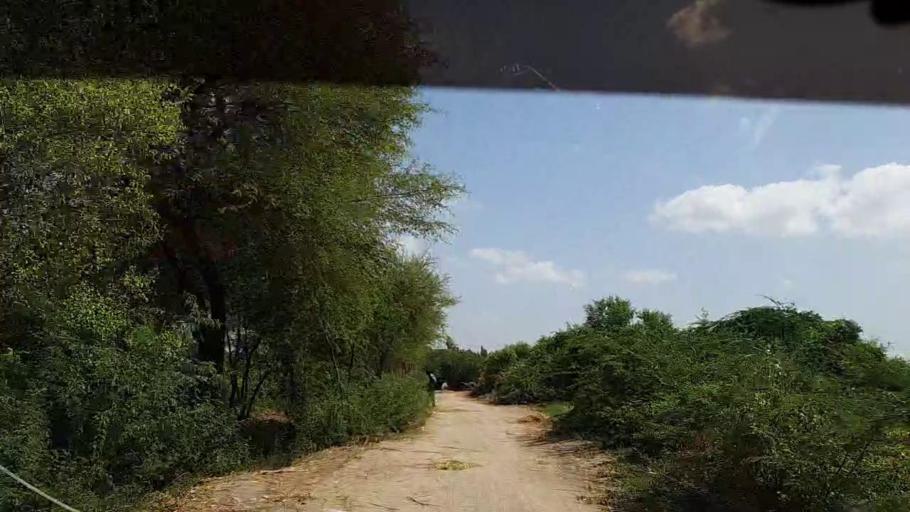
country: PK
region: Sindh
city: Badin
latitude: 24.5908
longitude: 68.8020
